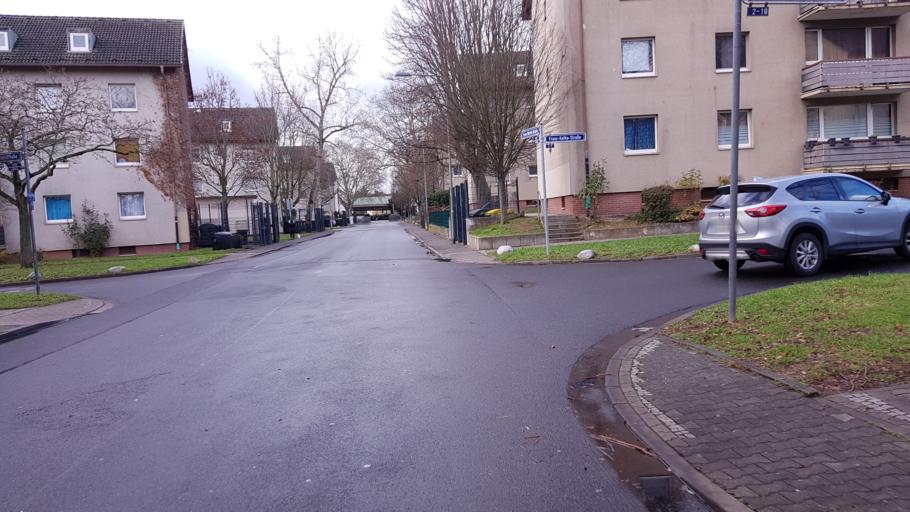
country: DE
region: Hesse
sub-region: Regierungsbezirk Darmstadt
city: Frankfurt am Main
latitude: 50.1381
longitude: 8.6575
